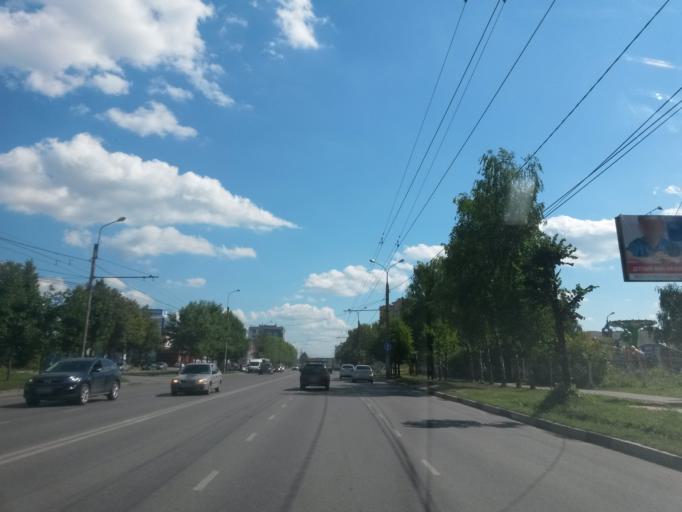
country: RU
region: Ivanovo
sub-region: Gorod Ivanovo
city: Ivanovo
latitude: 56.9681
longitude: 41.0177
